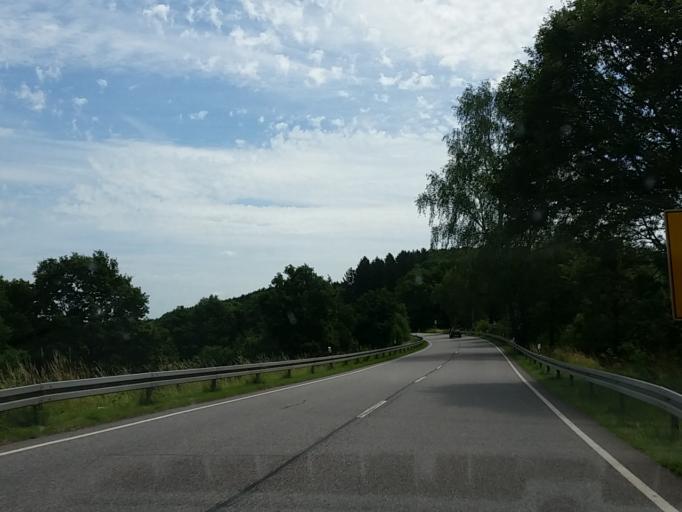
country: DE
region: Saarland
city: Britten
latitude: 49.5258
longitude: 6.6938
